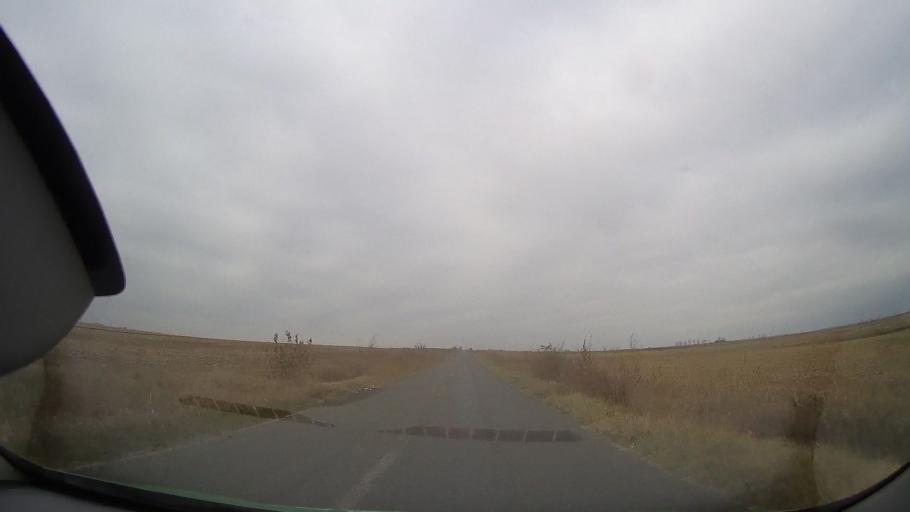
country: RO
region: Buzau
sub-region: Comuna Luciu
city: Luciu
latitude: 44.9769
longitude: 27.0575
